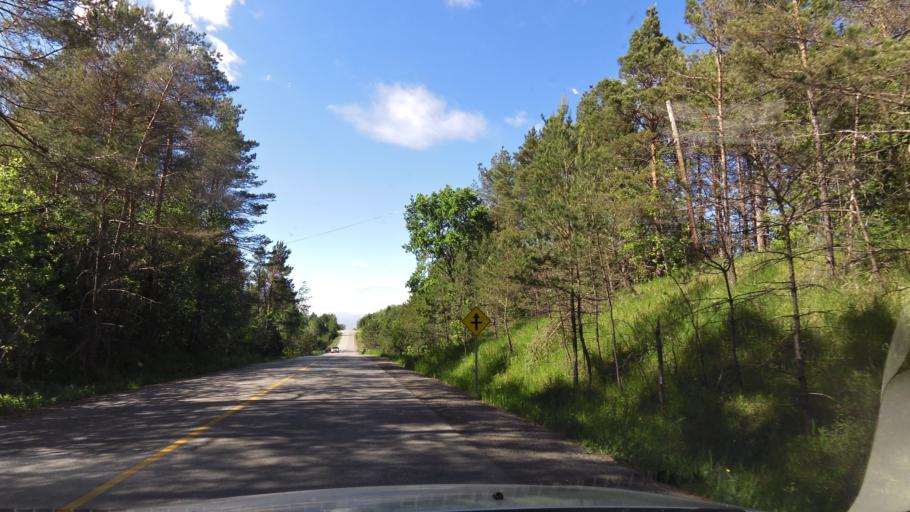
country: CA
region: Ontario
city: Bradford West Gwillimbury
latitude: 44.1885
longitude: -79.6221
